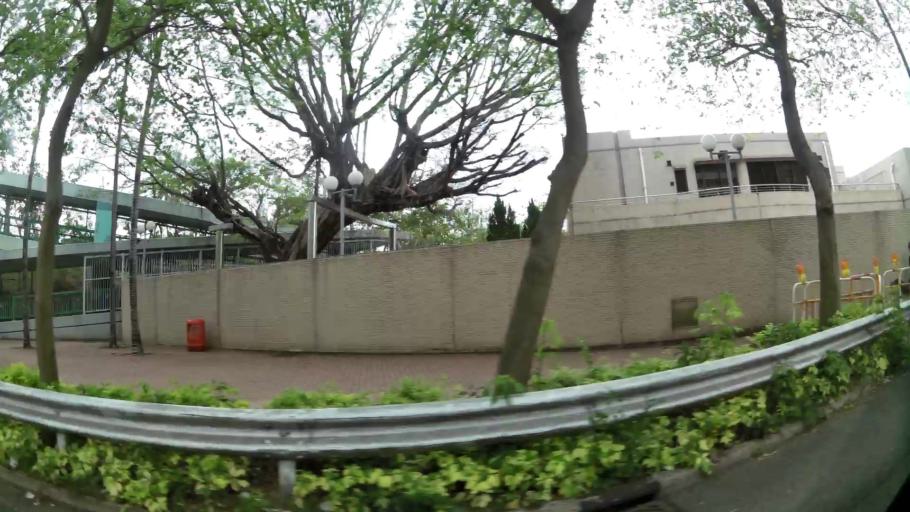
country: HK
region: Kowloon City
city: Kowloon
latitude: 22.3268
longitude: 114.1751
